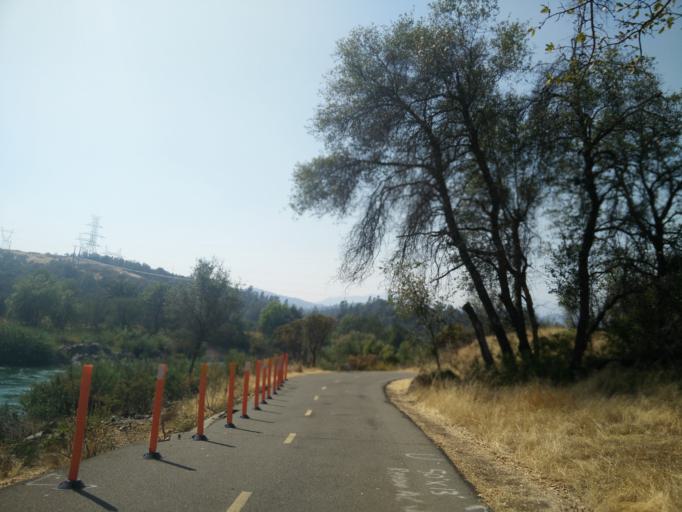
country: US
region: California
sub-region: Shasta County
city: Redding
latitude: 40.5947
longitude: -122.4321
